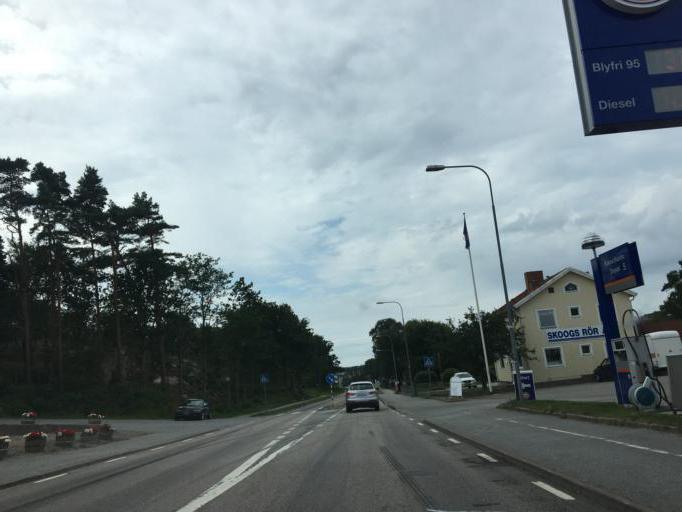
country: SE
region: Vaestra Goetaland
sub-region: Sotenas Kommun
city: Hunnebostrand
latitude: 58.4382
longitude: 11.3028
